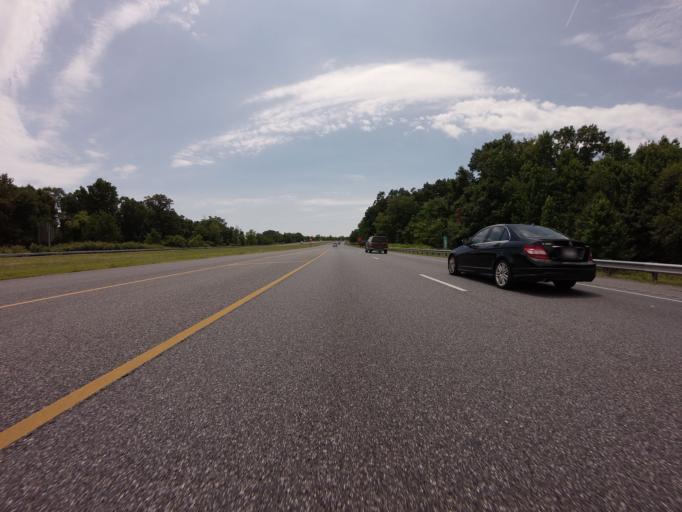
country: US
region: Maryland
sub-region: Baltimore County
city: Essex
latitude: 39.3192
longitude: -76.4884
